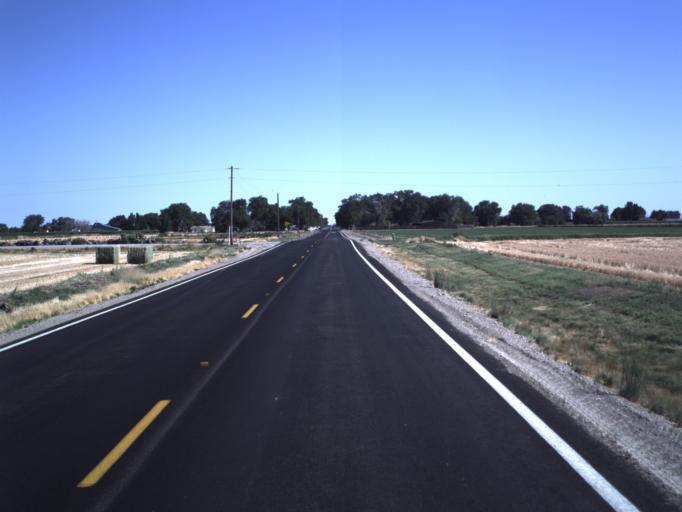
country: US
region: Utah
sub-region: Millard County
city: Delta
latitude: 39.2787
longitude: -112.6529
